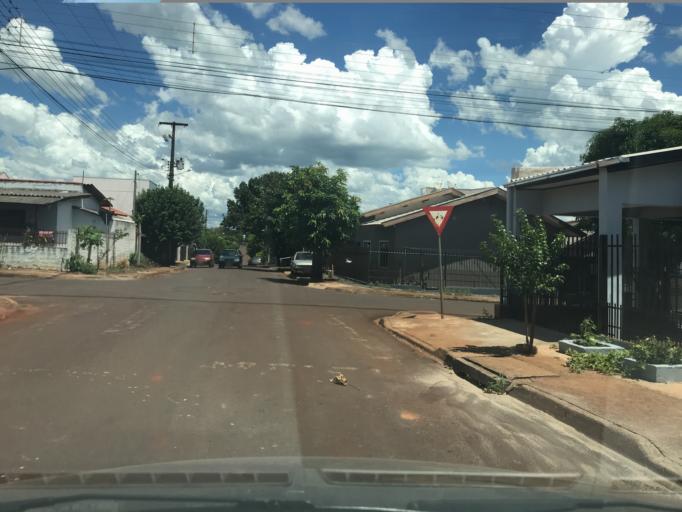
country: BR
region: Parana
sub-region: Palotina
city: Palotina
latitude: -24.2742
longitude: -53.8463
